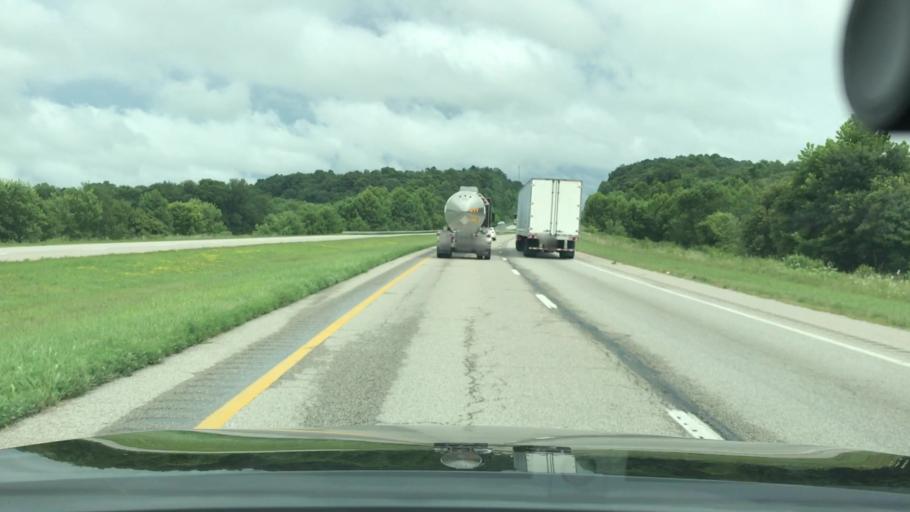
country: US
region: Ohio
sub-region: Gallia County
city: Gallipolis
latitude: 38.8930
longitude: -82.3616
